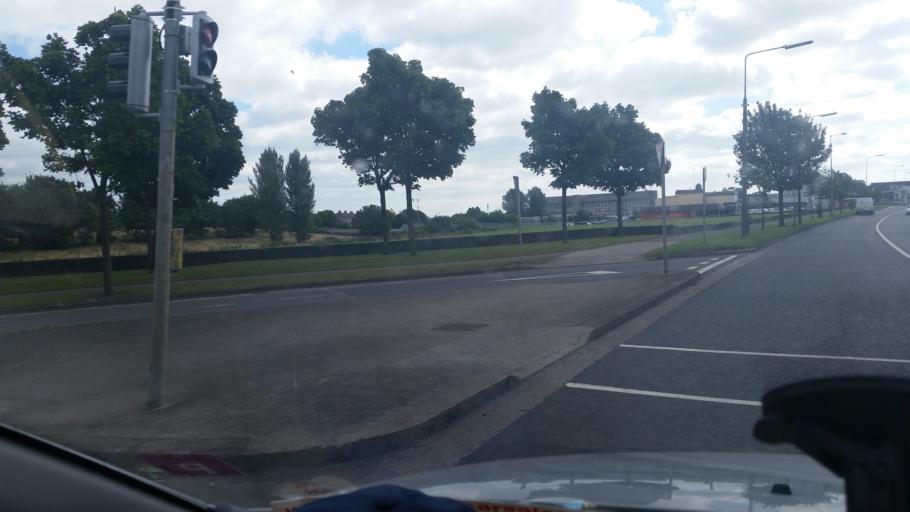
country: IE
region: Leinster
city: Artane
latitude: 53.3973
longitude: -6.2197
